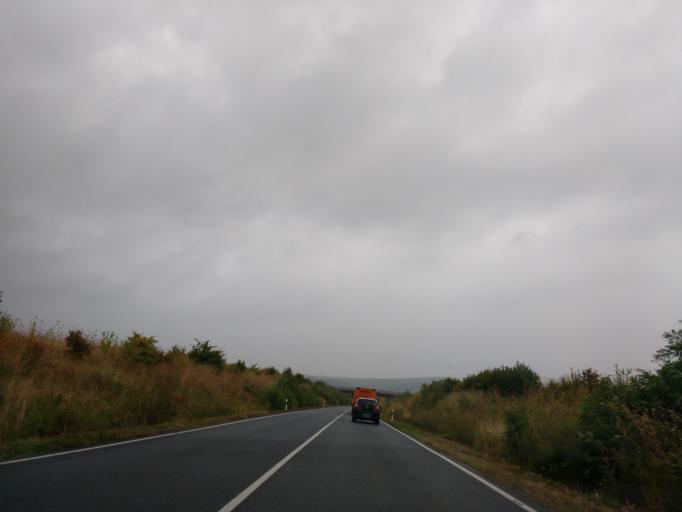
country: DE
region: Lower Saxony
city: Heinsen
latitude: 52.1121
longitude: 9.6832
